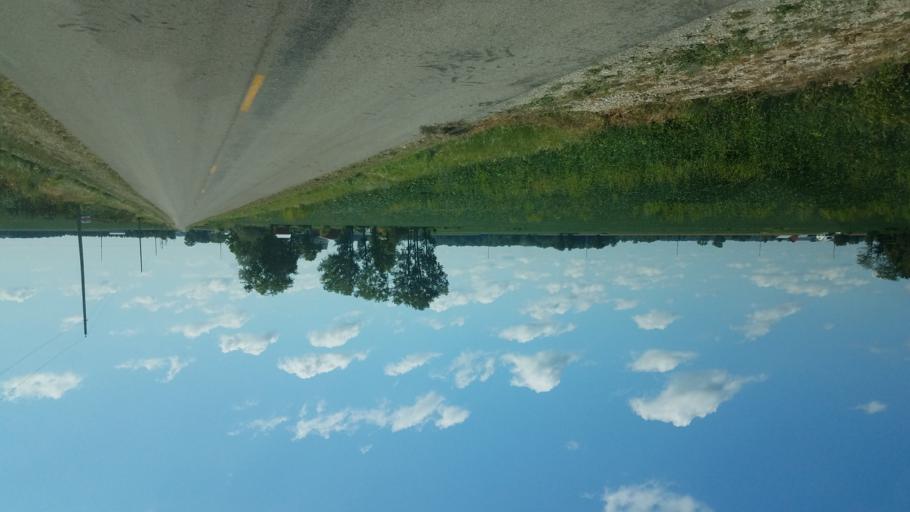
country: US
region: Ohio
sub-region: Wyandot County
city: Carey
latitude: 40.9853
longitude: -83.3100
